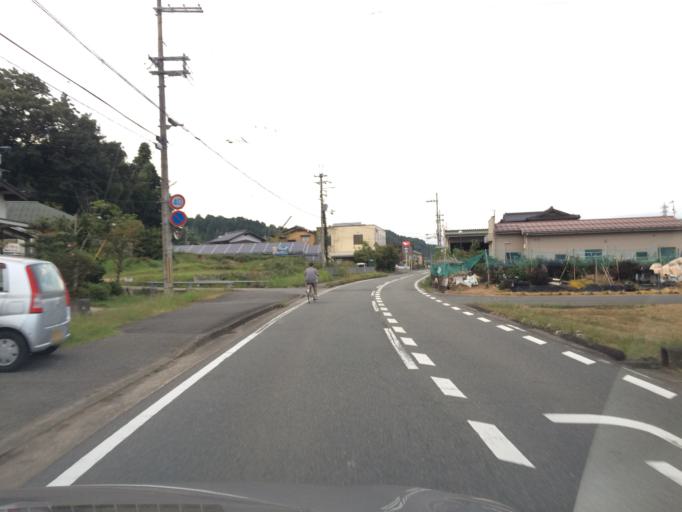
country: JP
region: Hyogo
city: Toyooka
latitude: 35.5243
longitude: 134.8179
